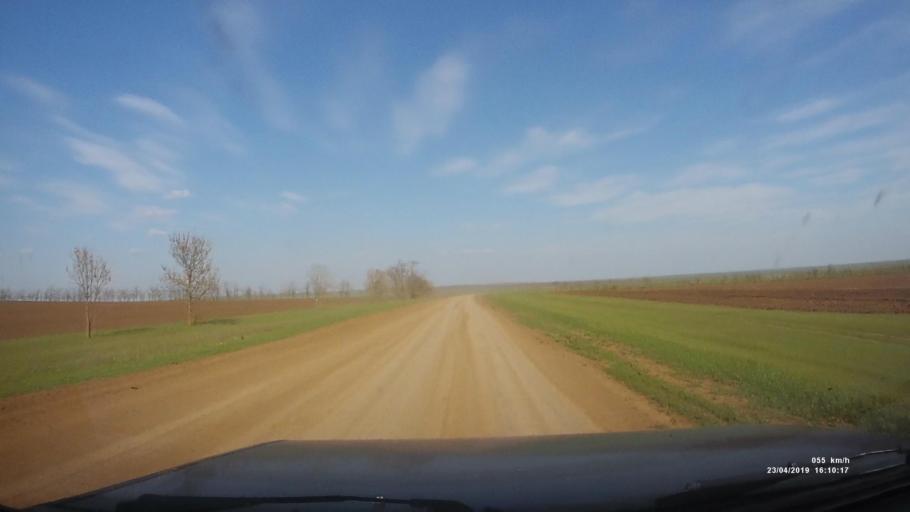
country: RU
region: Rostov
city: Remontnoye
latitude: 46.4815
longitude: 43.1200
